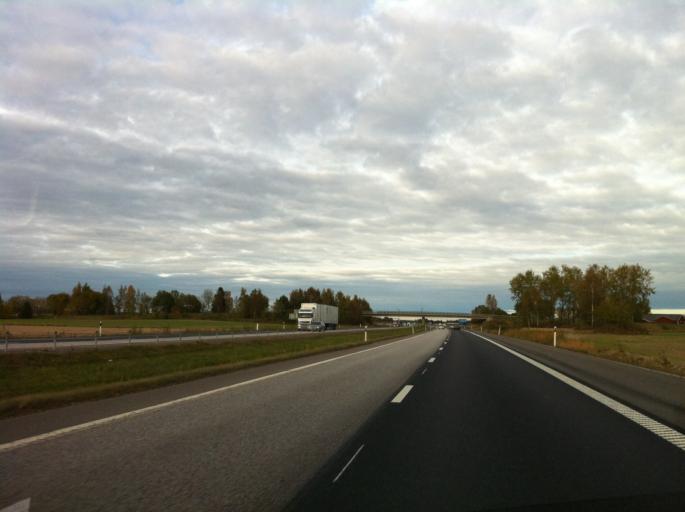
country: SE
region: OErebro
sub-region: Kumla Kommun
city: Kumla
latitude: 59.1261
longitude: 15.0737
